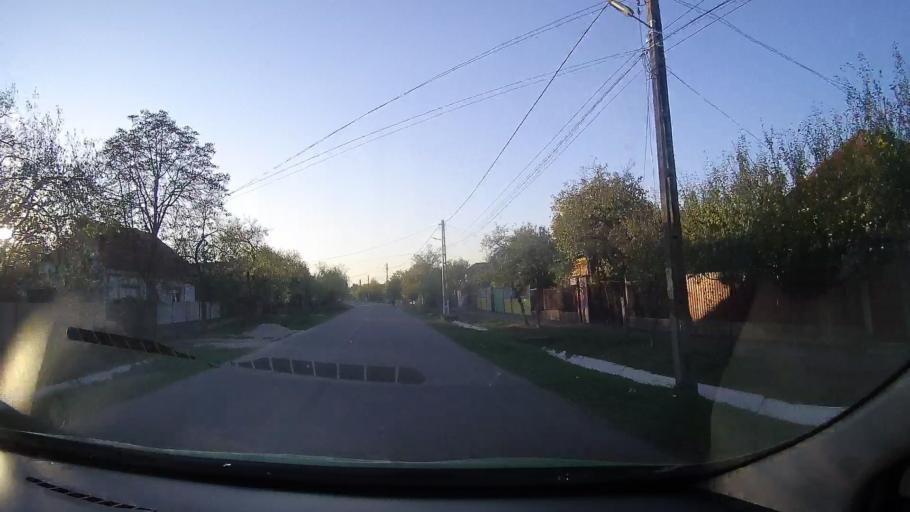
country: RO
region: Bihor
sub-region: Comuna Salard
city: Salard
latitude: 47.2226
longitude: 22.0351
